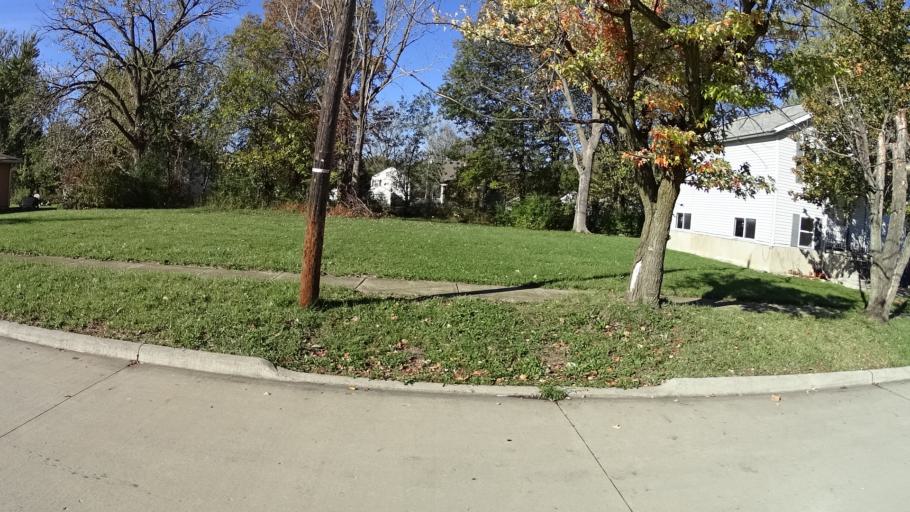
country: US
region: Ohio
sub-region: Lorain County
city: Lorain
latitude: 41.4347
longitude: -82.1552
